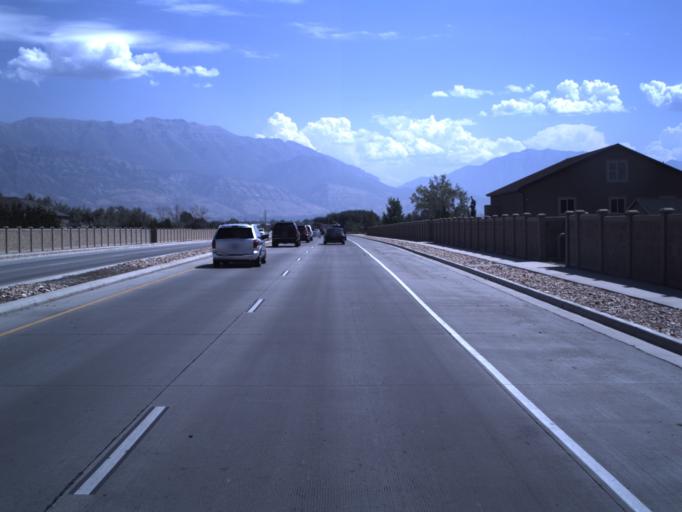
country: US
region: Utah
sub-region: Utah County
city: Lehi
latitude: 40.3737
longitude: -111.8549
